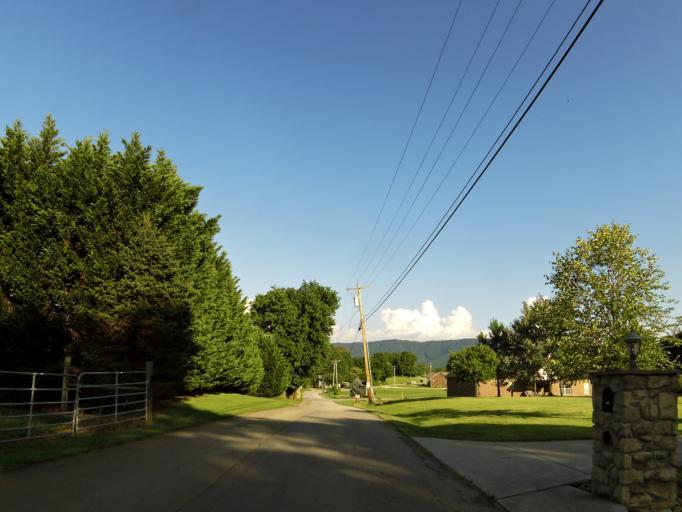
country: US
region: Tennessee
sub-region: Blount County
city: Wildwood
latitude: 35.7511
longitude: -83.8816
